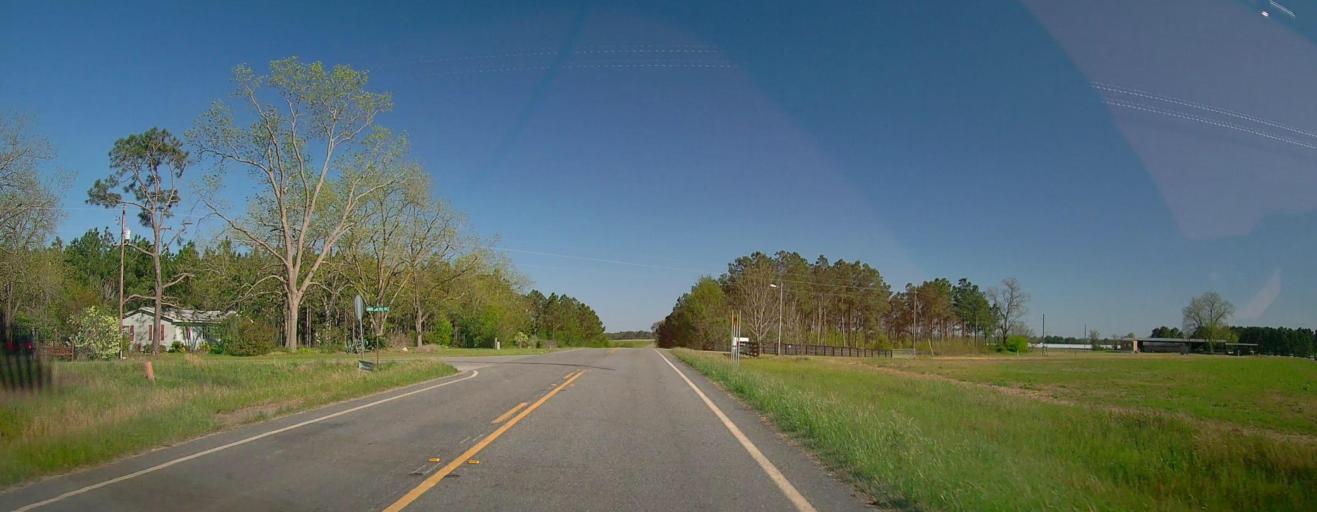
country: US
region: Georgia
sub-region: Wilcox County
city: Rochelle
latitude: 31.9897
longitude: -83.4663
